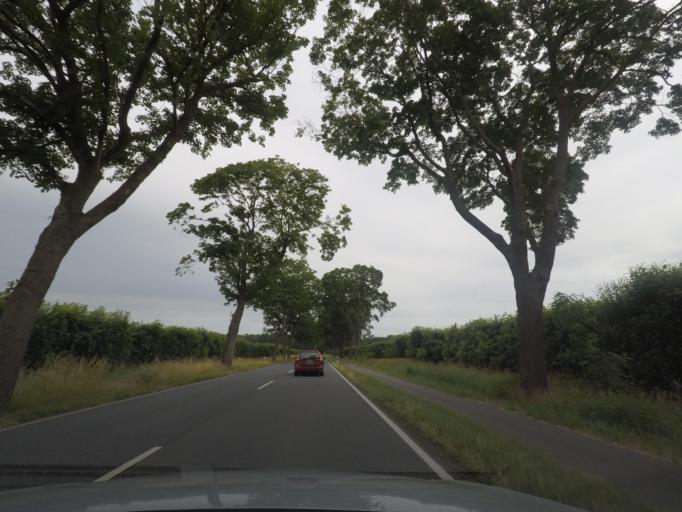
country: DE
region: Lower Saxony
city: Didderse
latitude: 52.3917
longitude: 10.3735
